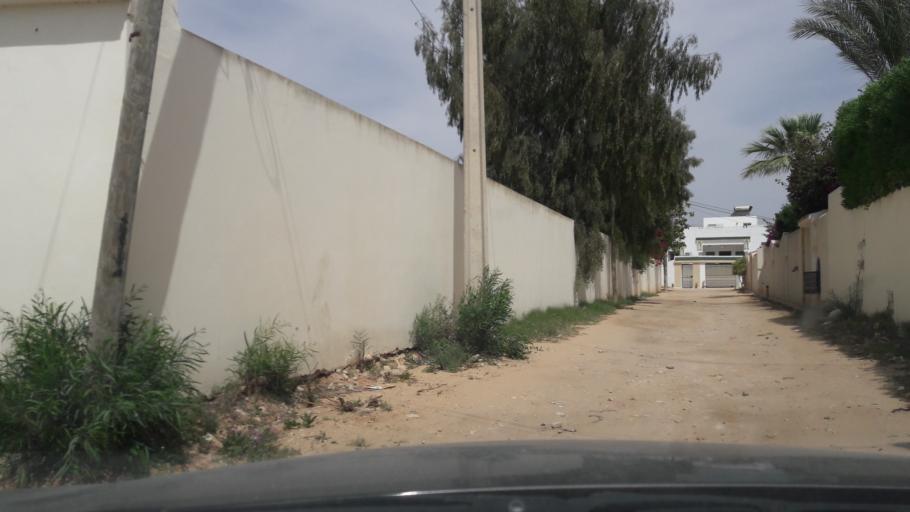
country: TN
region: Safaqis
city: Al Qarmadah
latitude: 34.7851
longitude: 10.7563
